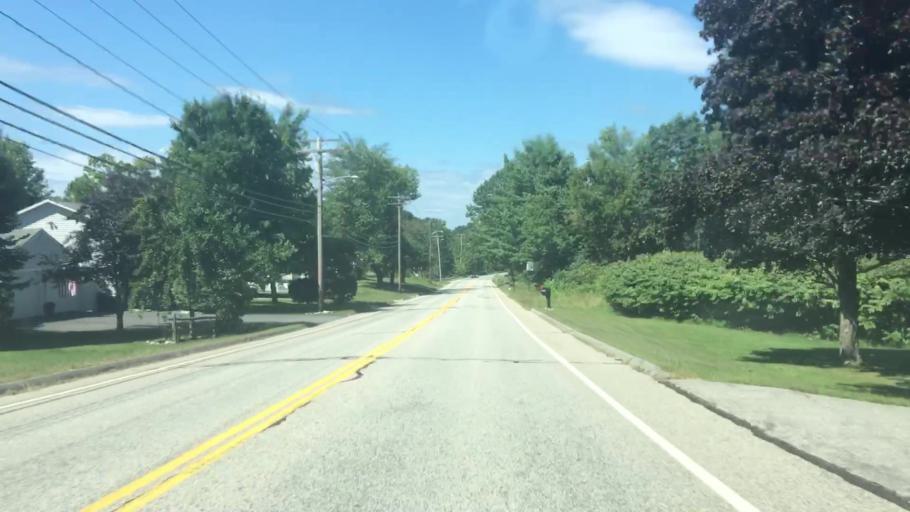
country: US
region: Maine
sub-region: Androscoggin County
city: Sabattus
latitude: 44.0890
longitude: -70.1445
